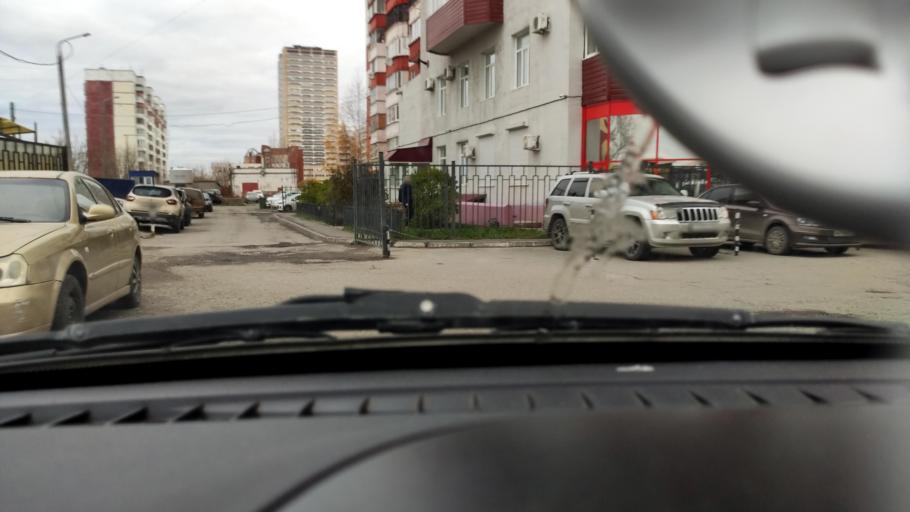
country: RU
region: Perm
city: Kondratovo
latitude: 57.9924
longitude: 56.1351
